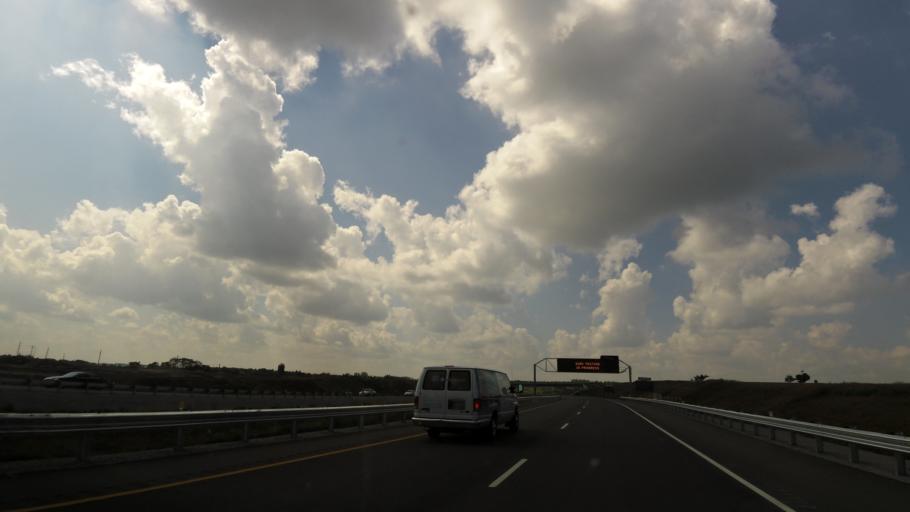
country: CA
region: Ontario
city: Ajax
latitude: 43.9508
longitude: -78.9793
